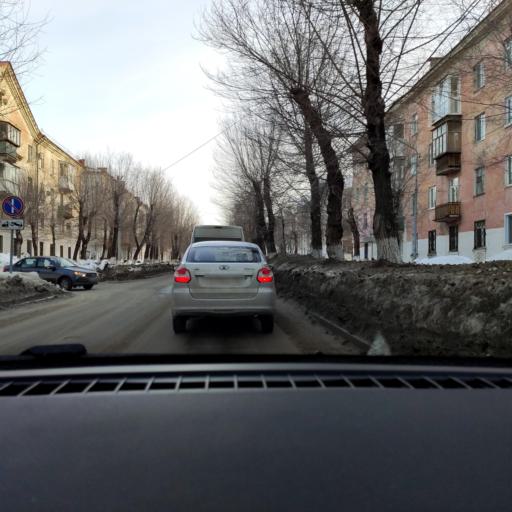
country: RU
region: Samara
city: Novokuybyshevsk
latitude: 53.0968
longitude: 49.9460
